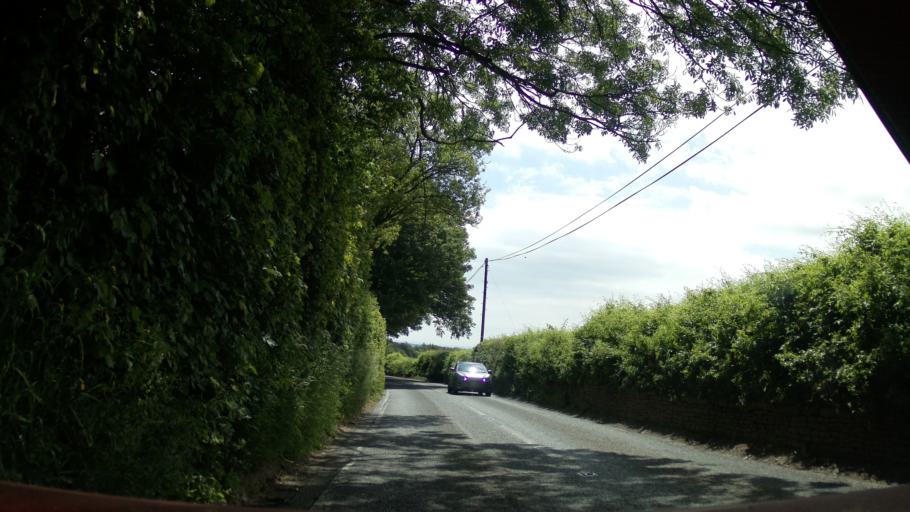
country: GB
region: England
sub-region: Somerset
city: Wincanton
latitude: 51.0556
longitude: -2.4485
